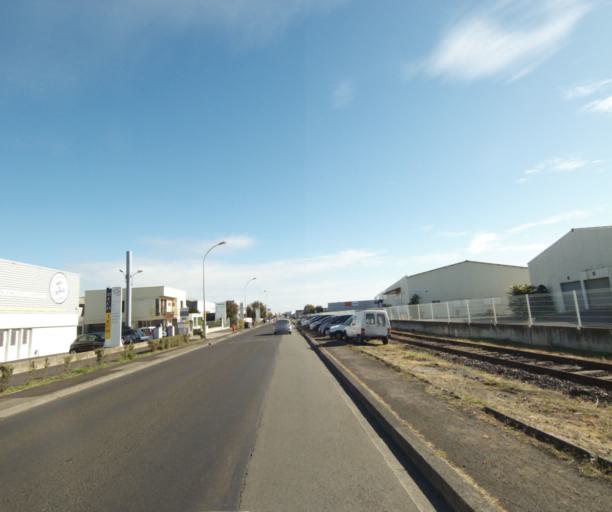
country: FR
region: Auvergne
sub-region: Departement du Puy-de-Dome
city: Aubiere
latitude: 45.7832
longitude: 3.1294
